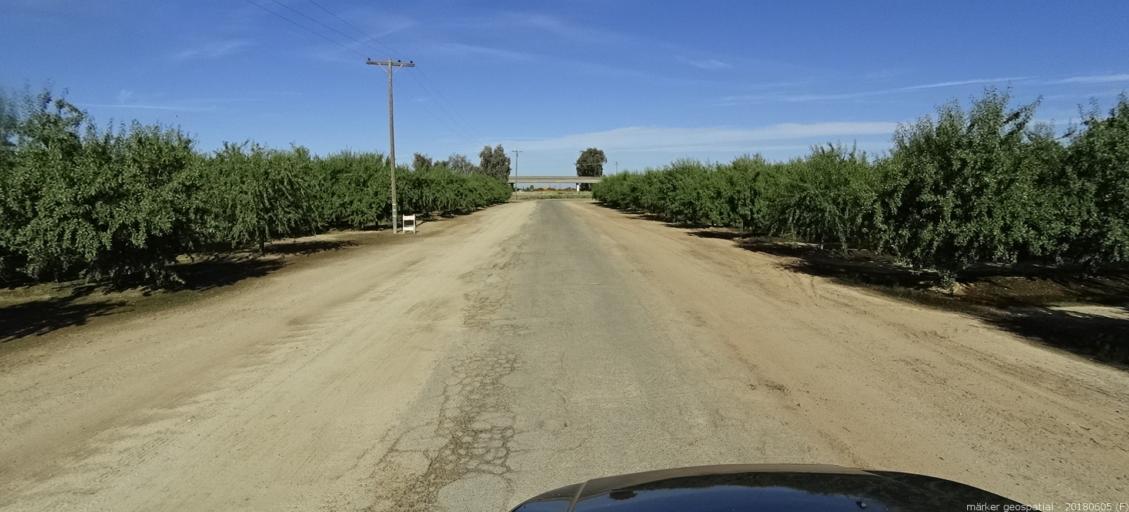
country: US
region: California
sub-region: Madera County
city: Chowchilla
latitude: 37.1419
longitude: -120.2717
